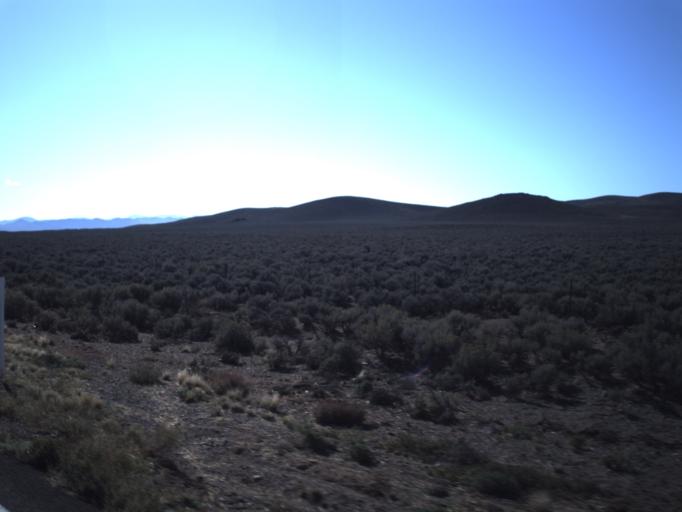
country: US
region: Utah
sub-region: Washington County
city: Enterprise
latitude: 37.7381
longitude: -113.7359
